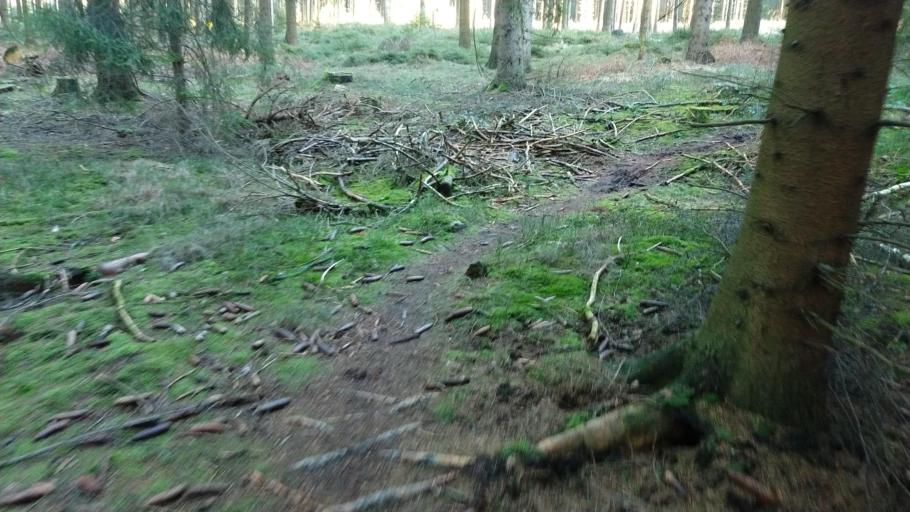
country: DE
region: Lower Saxony
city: Nienstadt
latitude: 52.2638
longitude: 9.1675
